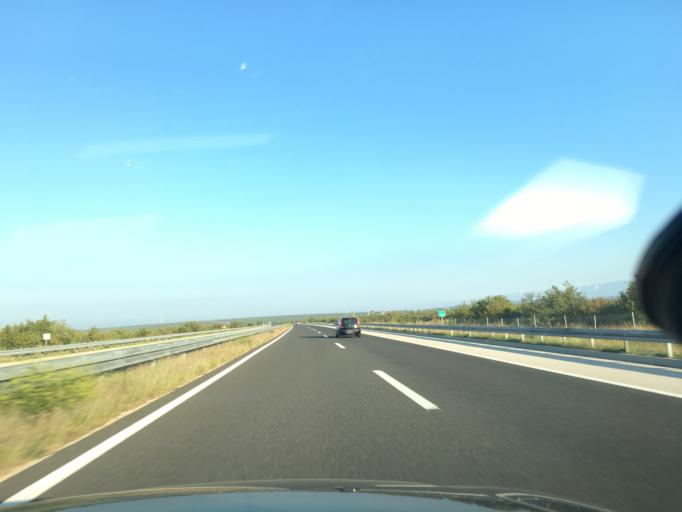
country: HR
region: Zadarska
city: Benkovac
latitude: 43.9839
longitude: 15.6327
